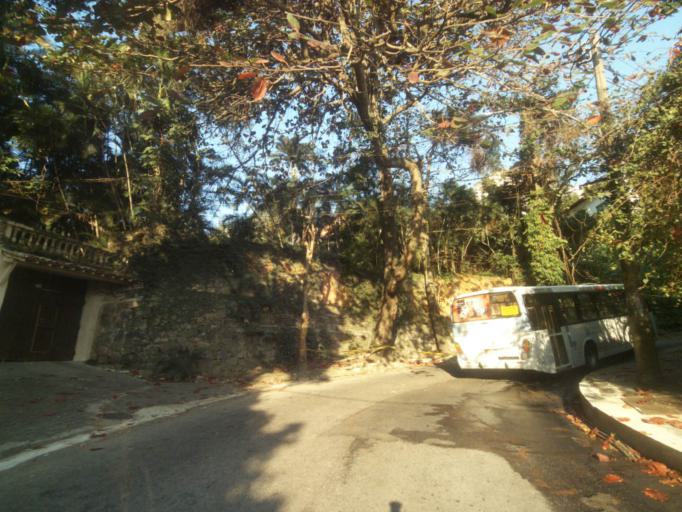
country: BR
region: Rio de Janeiro
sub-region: Rio De Janeiro
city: Rio de Janeiro
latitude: -23.0081
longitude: -43.2902
